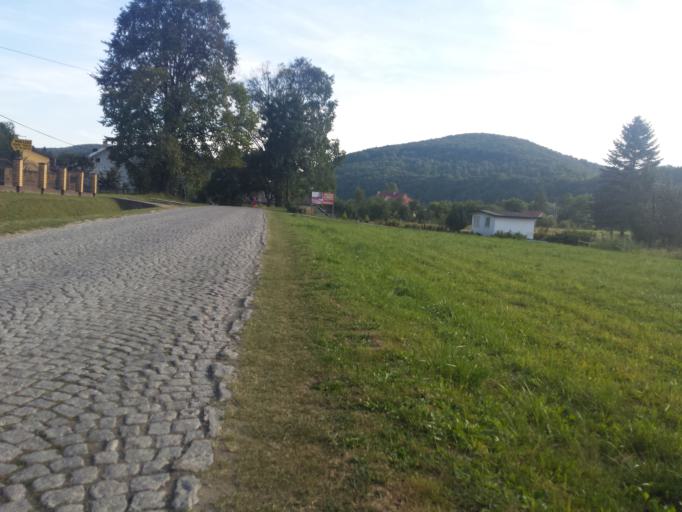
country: PL
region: Subcarpathian Voivodeship
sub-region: Powiat leski
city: Uherce Mineralne
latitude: 49.4379
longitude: 22.4103
